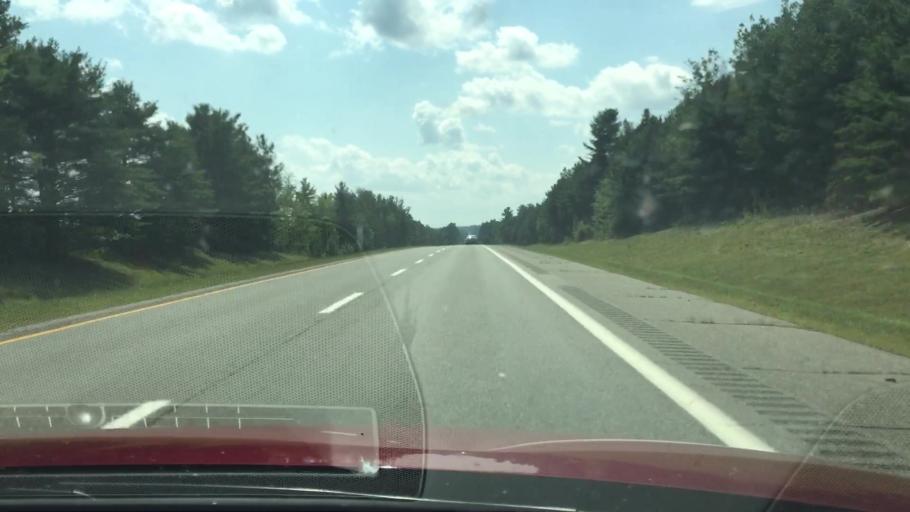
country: US
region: Maine
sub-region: Penobscot County
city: Medway
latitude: 45.4958
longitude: -68.5626
